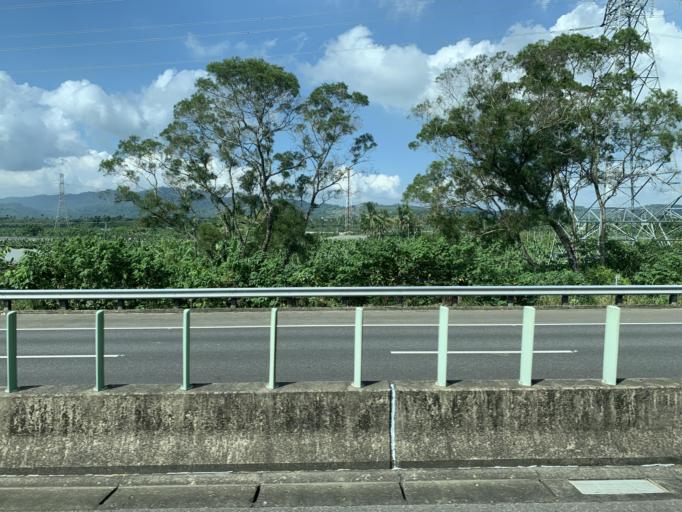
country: TW
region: Taiwan
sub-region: Pingtung
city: Pingtung
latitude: 22.8538
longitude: 120.4950
